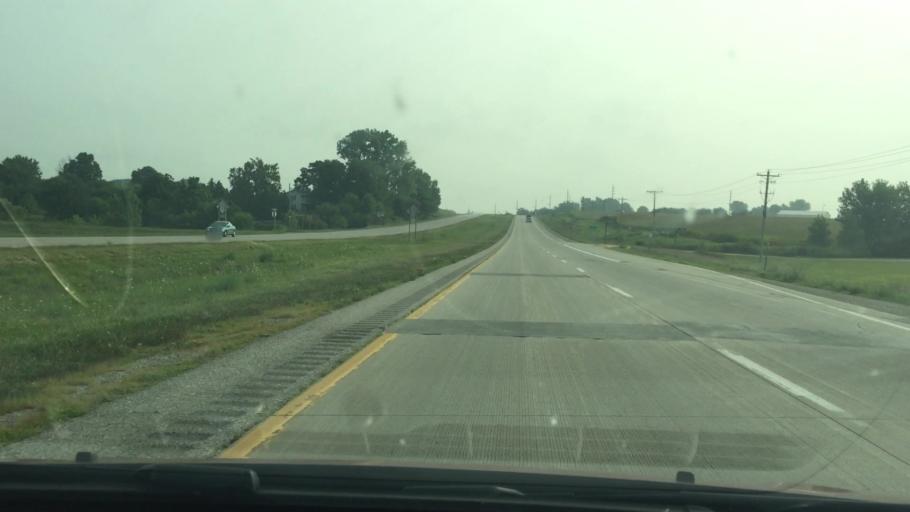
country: US
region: Iowa
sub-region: Muscatine County
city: Muscatine
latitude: 41.4607
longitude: -91.0147
